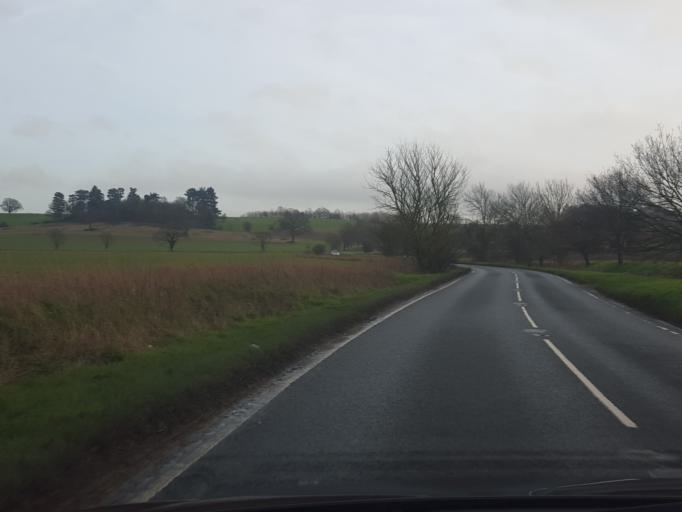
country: GB
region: England
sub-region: Essex
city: Eight Ash Green
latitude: 51.9575
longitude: 0.7923
